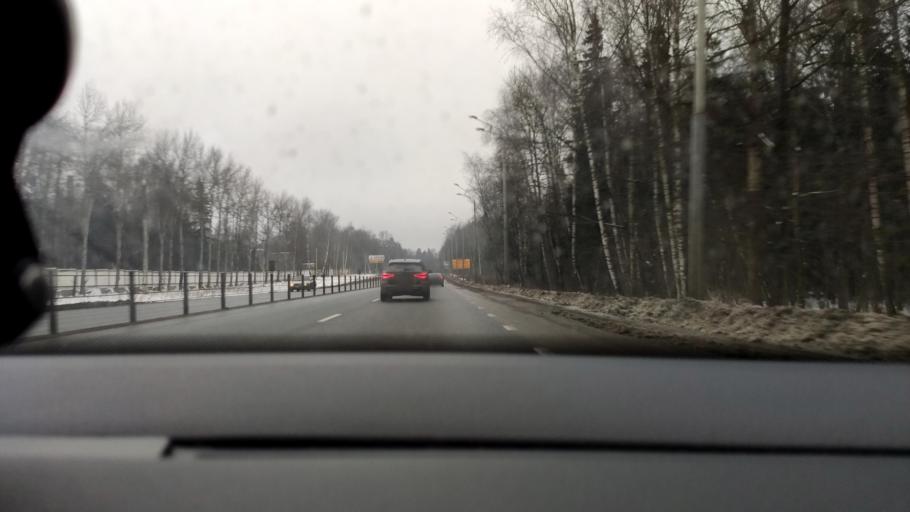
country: RU
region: Moskovskaya
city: Sergiyev Posad
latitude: 56.2552
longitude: 38.1252
